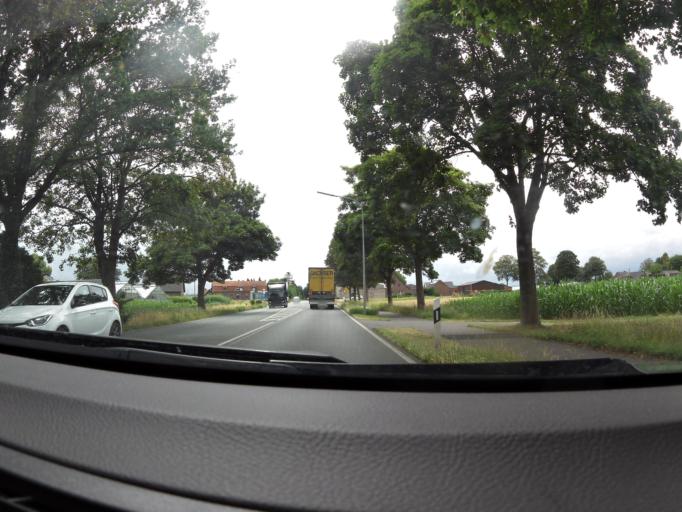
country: DE
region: North Rhine-Westphalia
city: Straelen
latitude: 51.4645
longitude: 6.2808
